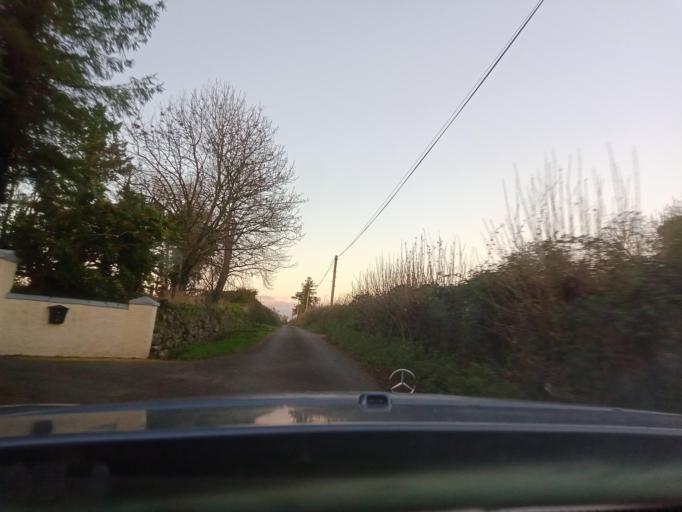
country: IE
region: Leinster
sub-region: Kilkenny
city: Graiguenamanagh
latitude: 52.5544
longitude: -6.9623
